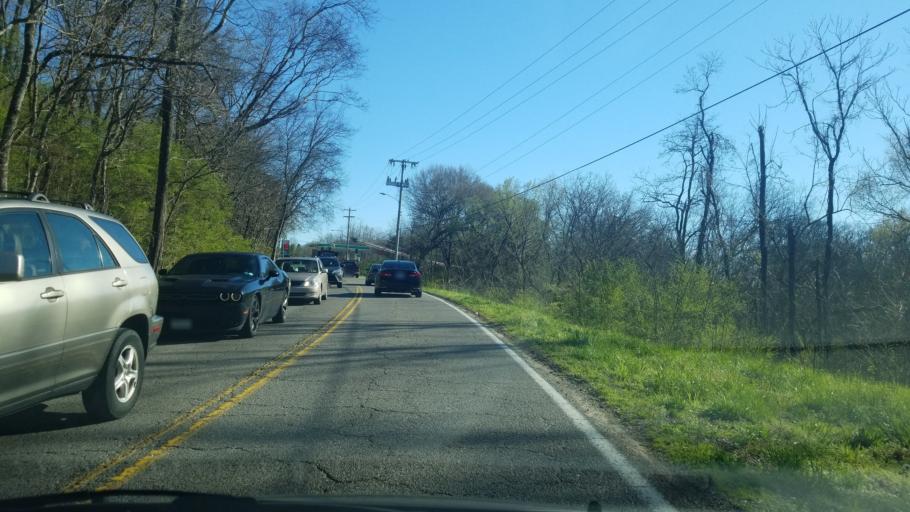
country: US
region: Tennessee
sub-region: Hamilton County
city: East Chattanooga
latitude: 35.1082
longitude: -85.2205
